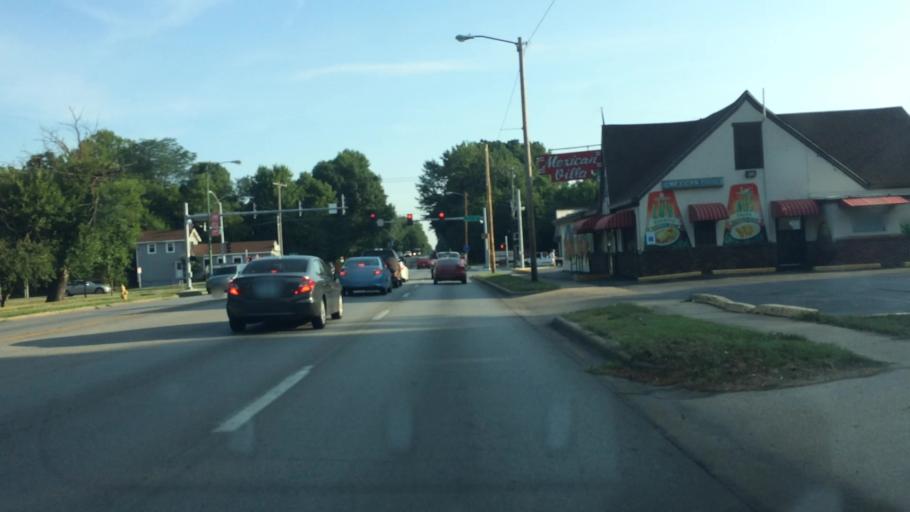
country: US
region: Missouri
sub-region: Greene County
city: Springfield
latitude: 37.1885
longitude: -93.2764
